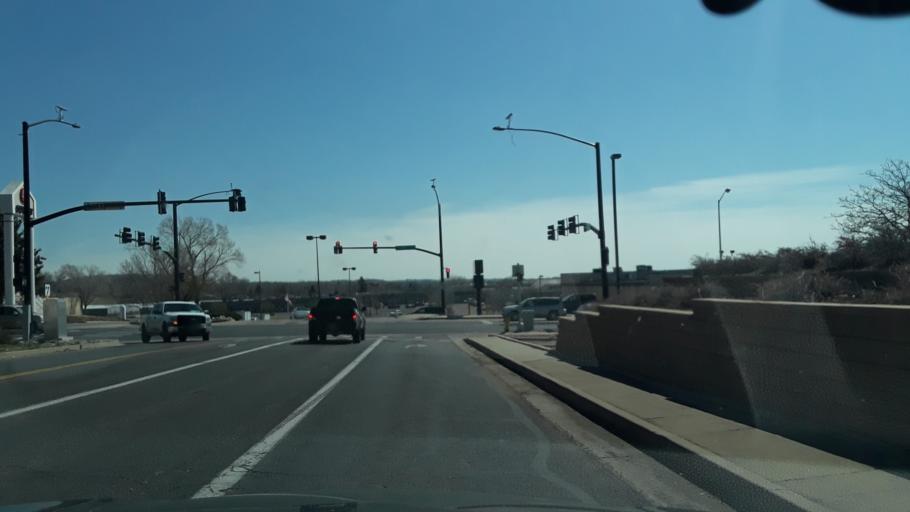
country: US
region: Colorado
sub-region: El Paso County
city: Colorado Springs
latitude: 38.8489
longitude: -104.7765
